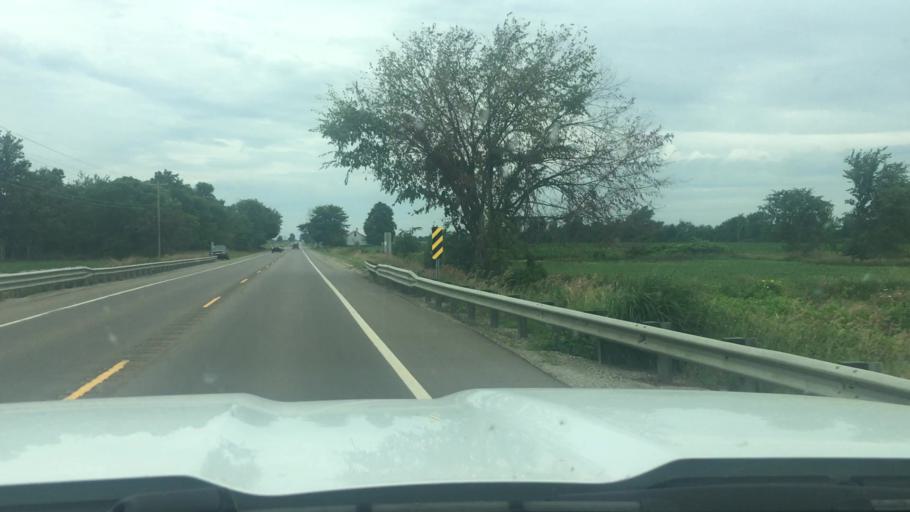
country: US
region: Michigan
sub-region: Clinton County
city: Fowler
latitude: 43.0018
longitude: -84.6836
